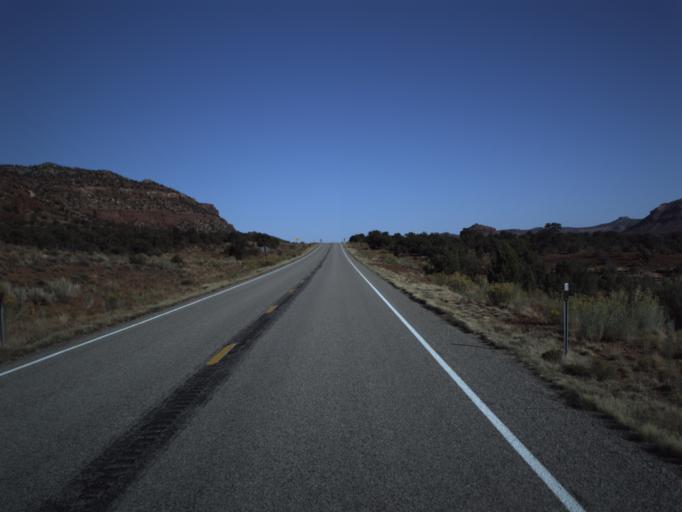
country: US
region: Utah
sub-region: San Juan County
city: Blanding
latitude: 37.6064
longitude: -110.0792
